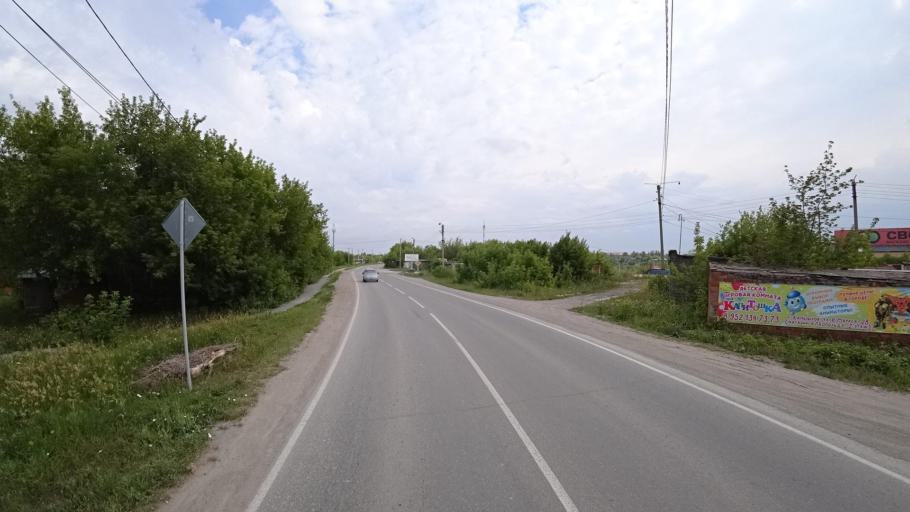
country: RU
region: Sverdlovsk
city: Kamyshlov
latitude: 56.8540
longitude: 62.7181
